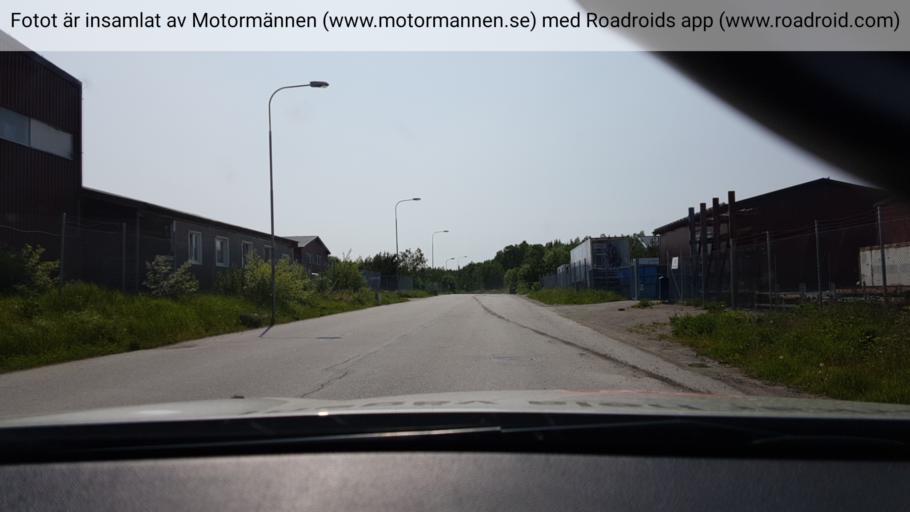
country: SE
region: Stockholm
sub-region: Nynashamns Kommun
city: Nynashamn
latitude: 58.9323
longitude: 17.9380
